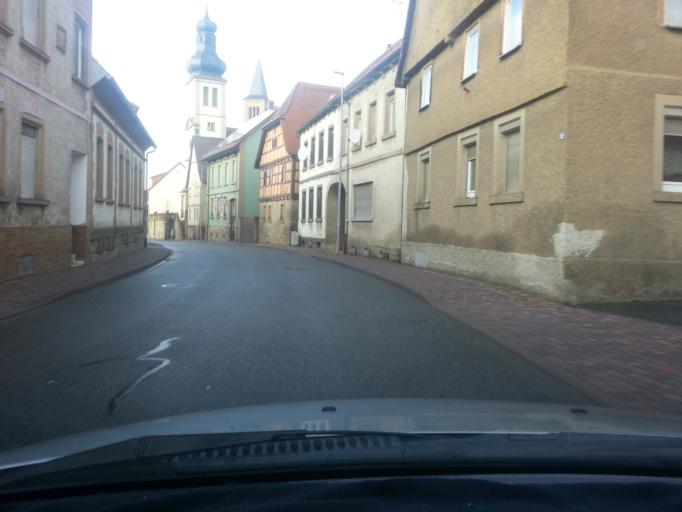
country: DE
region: Baden-Wuerttemberg
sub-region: Karlsruhe Region
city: Sulzfeld
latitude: 49.1741
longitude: 8.8377
